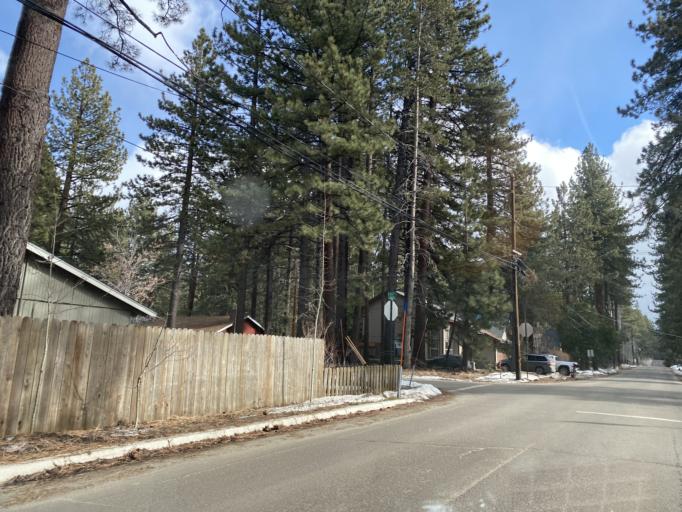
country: US
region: California
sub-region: El Dorado County
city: South Lake Tahoe
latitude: 38.9209
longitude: -119.9857
